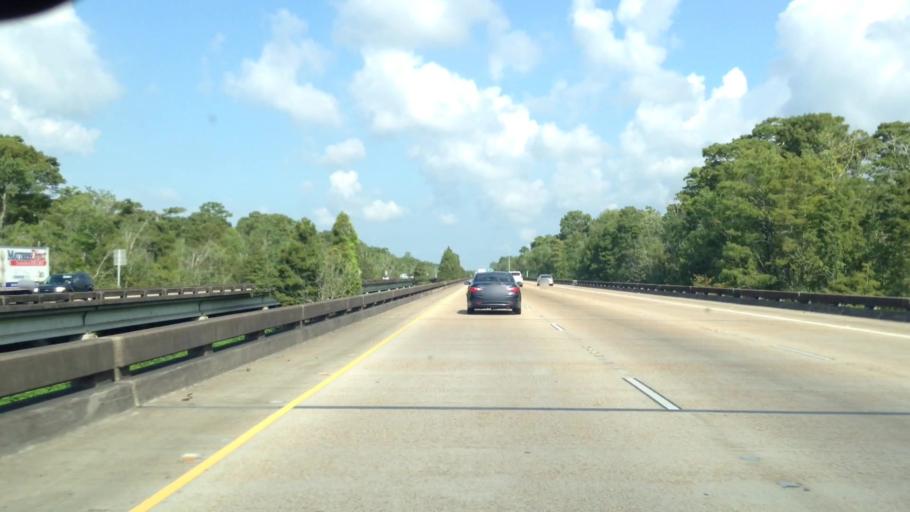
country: US
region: Louisiana
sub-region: Saint John the Baptist Parish
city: Laplace
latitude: 30.0825
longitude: -90.4205
